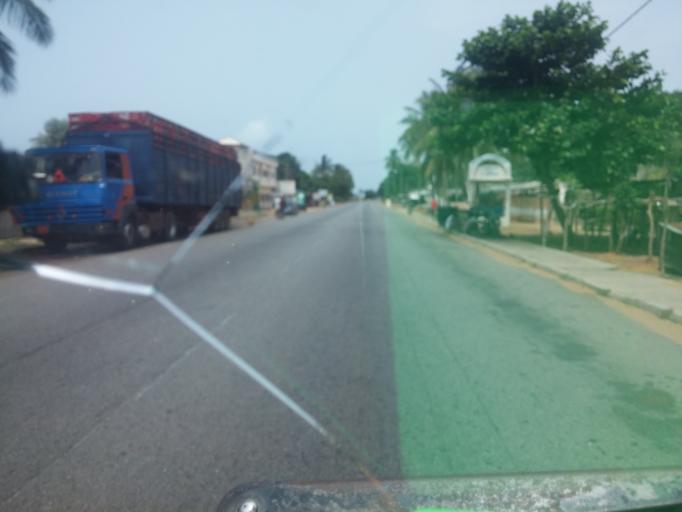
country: TG
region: Maritime
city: Aneho
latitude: 6.2093
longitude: 1.4789
